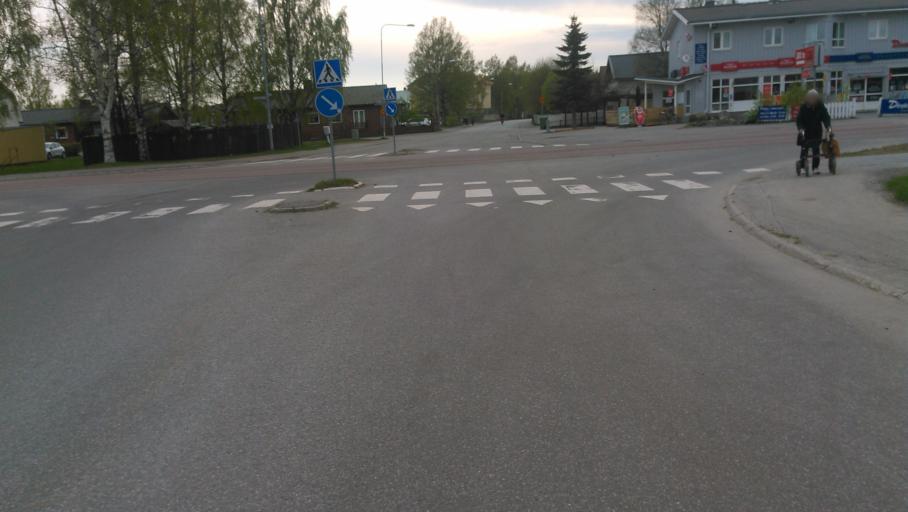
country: SE
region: Vaesterbotten
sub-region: Umea Kommun
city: Umea
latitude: 63.8107
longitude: 20.2696
